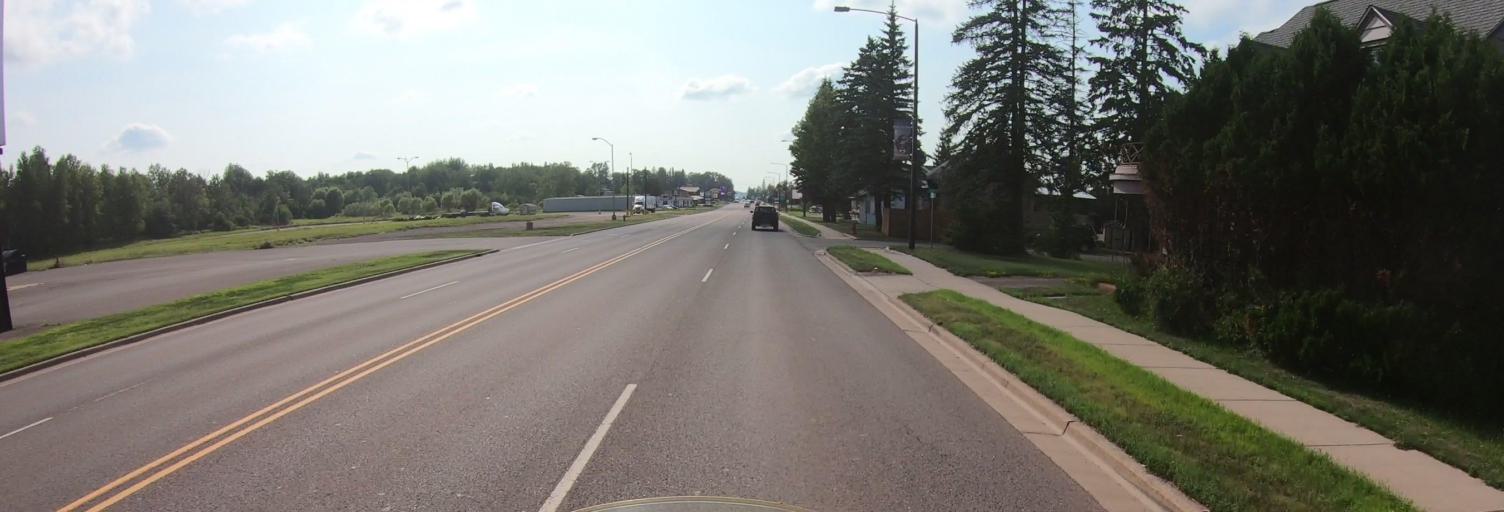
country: US
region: Michigan
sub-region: Gogebic County
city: Ironwood
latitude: 46.4633
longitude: -90.1497
